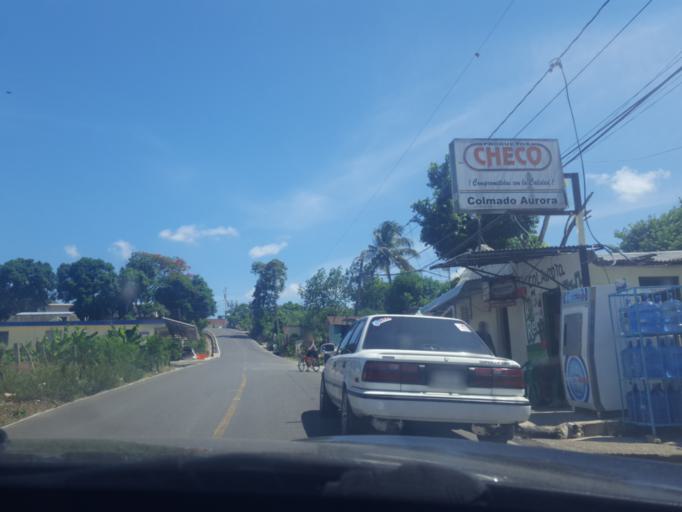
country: DO
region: Santiago
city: Licey al Medio
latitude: 19.3864
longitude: -70.6501
